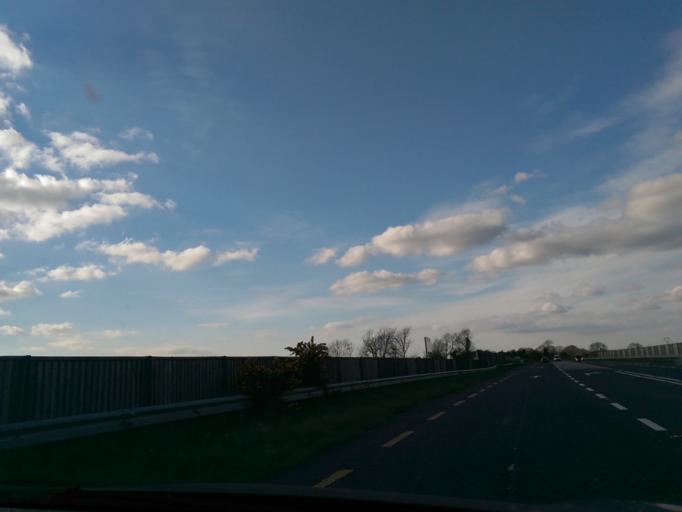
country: IE
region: Connaught
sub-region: County Galway
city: Loughrea
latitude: 53.2296
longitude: -8.5928
